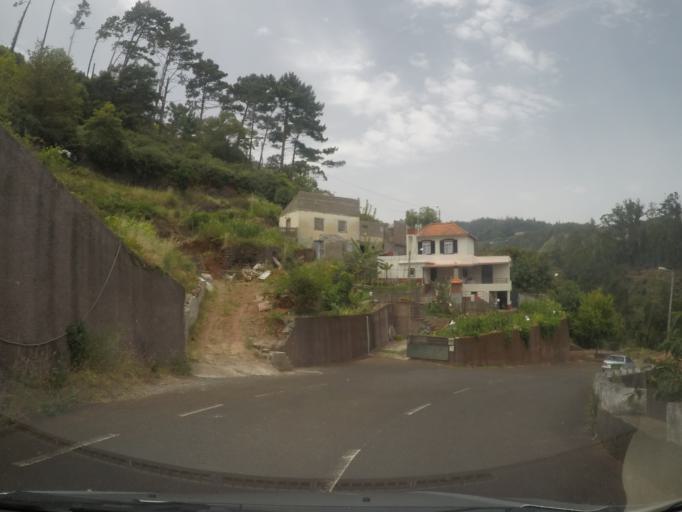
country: PT
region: Madeira
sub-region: Santa Cruz
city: Camacha
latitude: 32.6812
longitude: -16.8428
